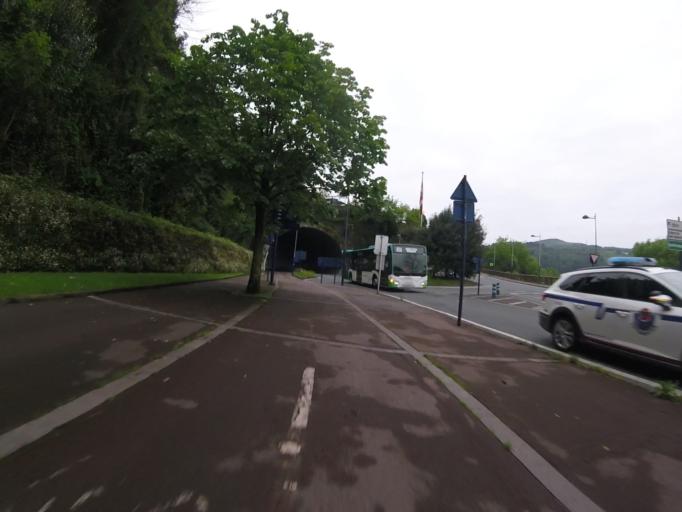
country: ES
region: Basque Country
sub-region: Provincia de Guipuzcoa
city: Errenteria
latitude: 43.3178
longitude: -1.9061
